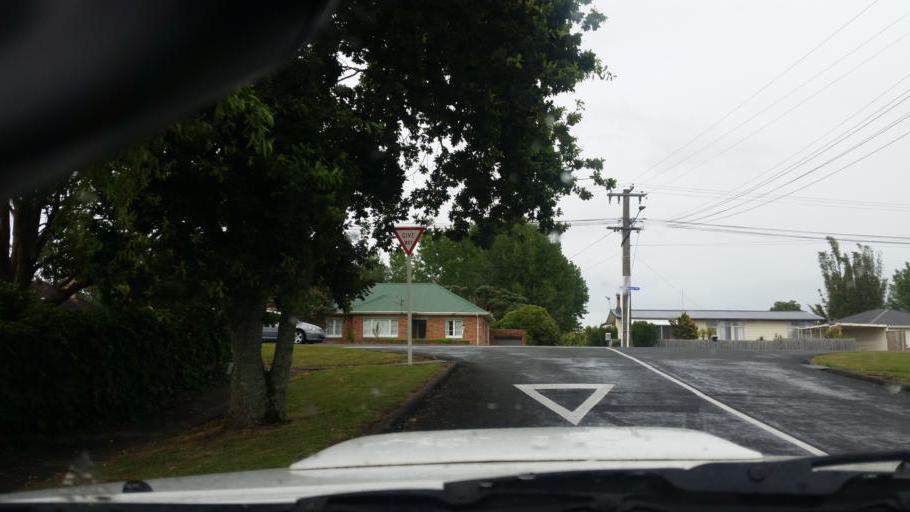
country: NZ
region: Northland
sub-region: Kaipara District
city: Dargaville
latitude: -35.9326
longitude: 173.8592
